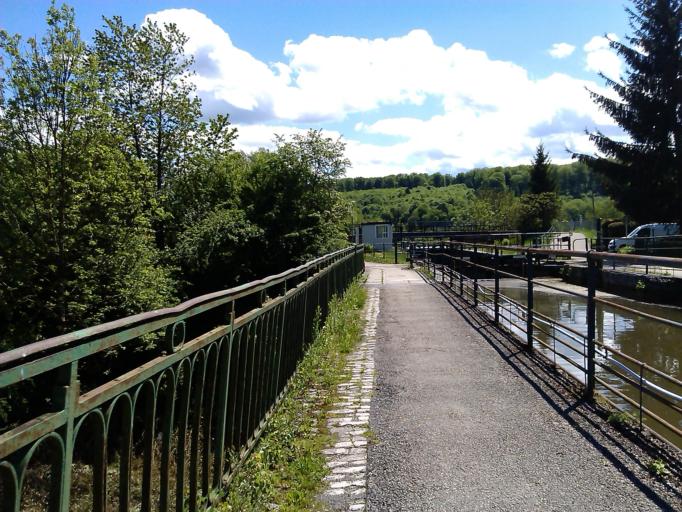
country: FR
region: Franche-Comte
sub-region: Departement du Doubs
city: Etupes
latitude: 47.5231
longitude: 6.8807
